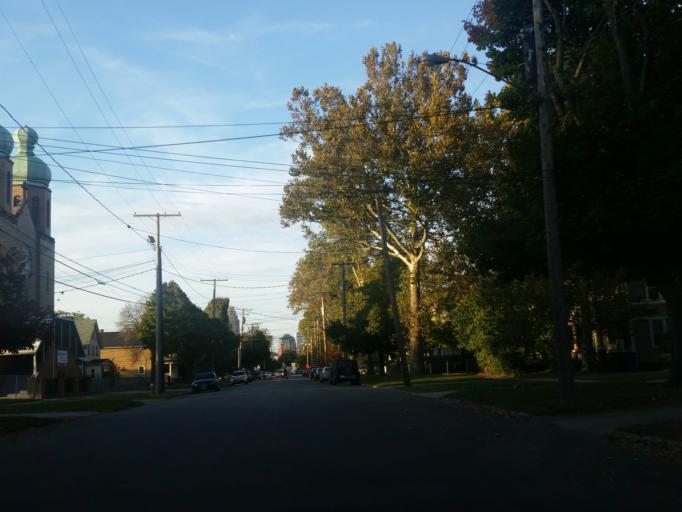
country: US
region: Ohio
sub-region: Cuyahoga County
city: Cleveland
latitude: 41.4805
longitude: -81.6893
